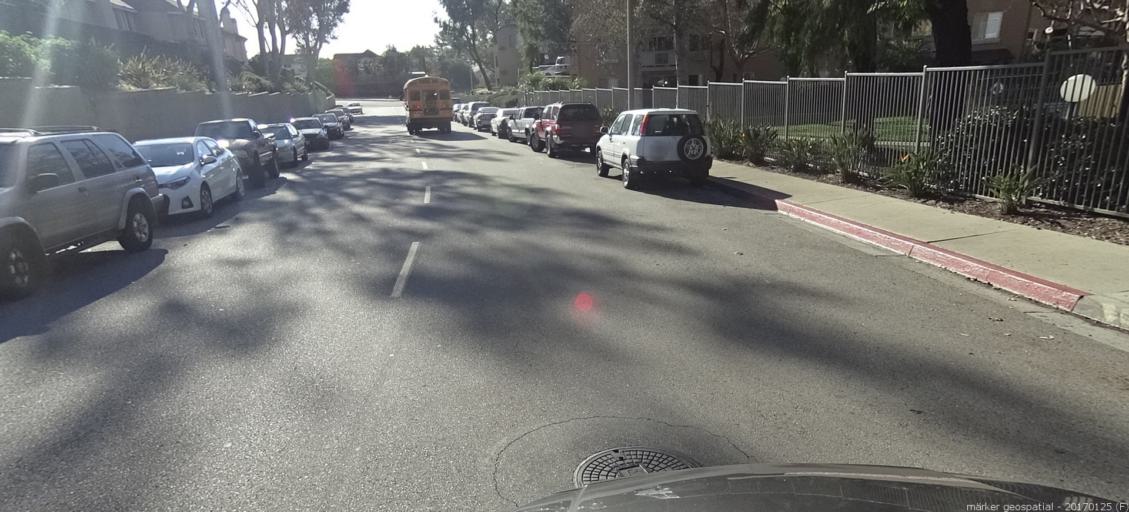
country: US
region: California
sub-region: Orange County
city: Lake Forest
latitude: 33.6406
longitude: -117.6812
